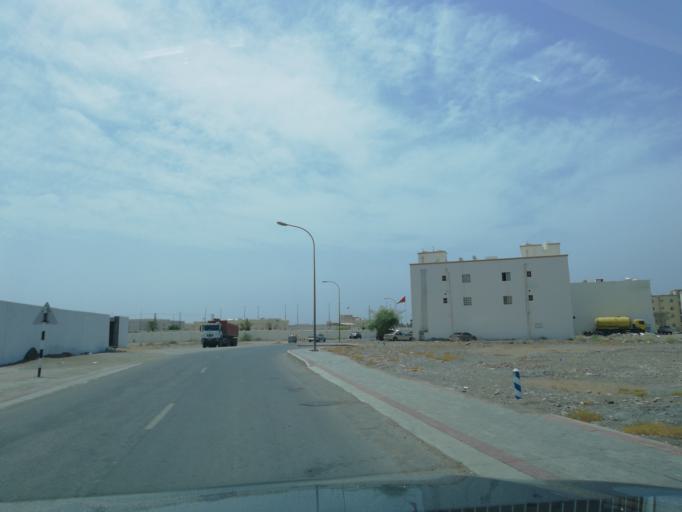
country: OM
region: Muhafazat Masqat
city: As Sib al Jadidah
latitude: 23.6625
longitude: 58.1946
